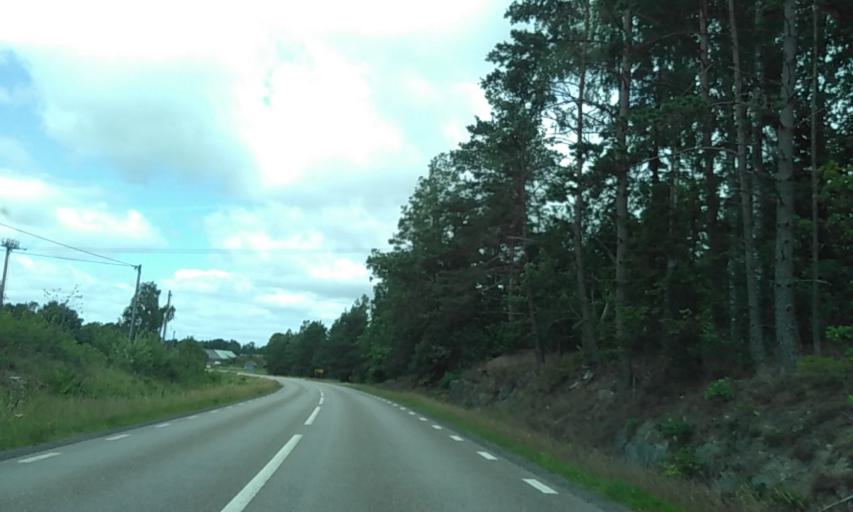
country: SE
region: Vaestra Goetaland
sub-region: Grastorps Kommun
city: Graestorp
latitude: 58.2731
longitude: 12.6819
